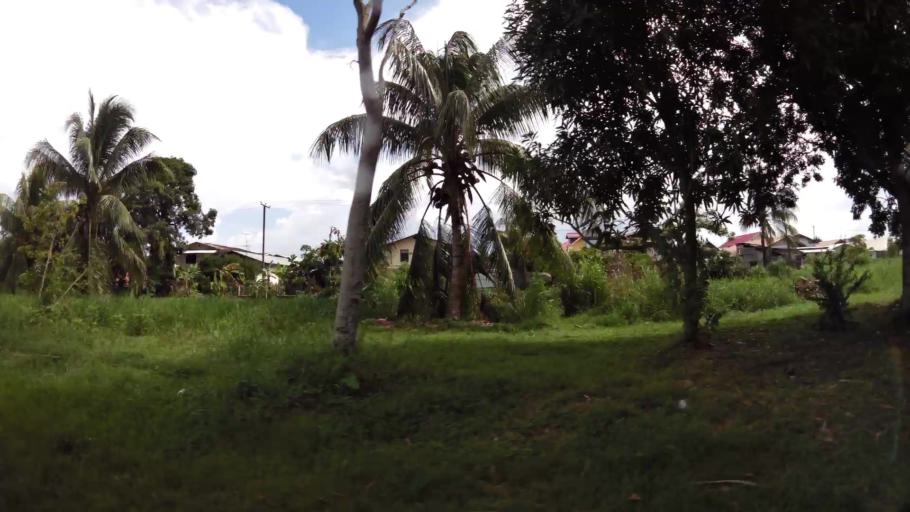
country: SR
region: Paramaribo
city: Paramaribo
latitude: 5.8465
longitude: -55.1495
